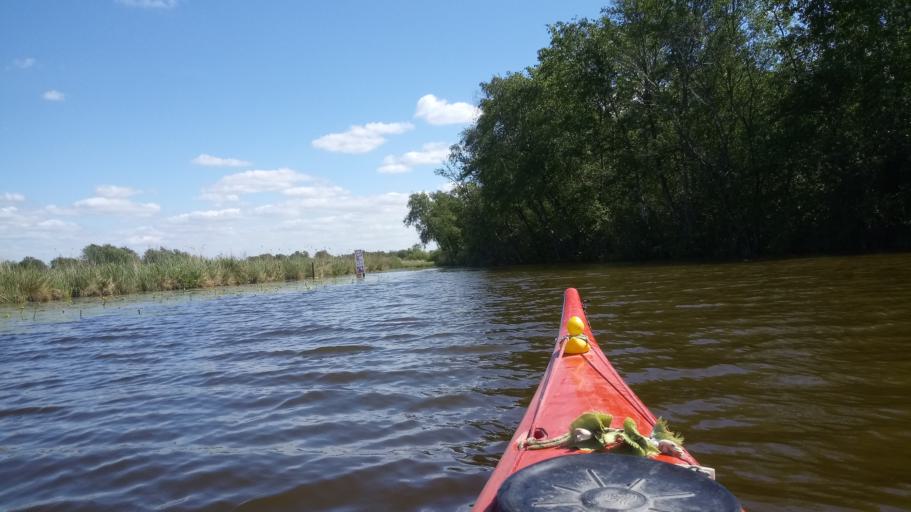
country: NL
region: South Holland
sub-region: Gemeente Nieuwkoop
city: Nieuwkoop
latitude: 52.1406
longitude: 4.7795
